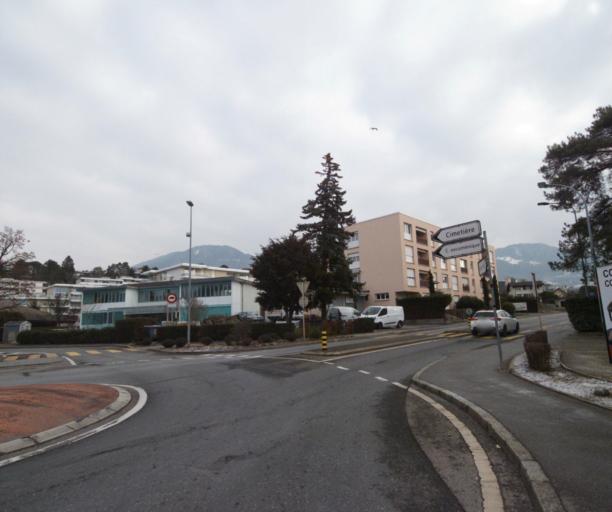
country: CH
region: Vaud
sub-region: Riviera-Pays-d'Enhaut District
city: La Tour-de-Peilz
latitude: 46.4569
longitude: 6.8646
